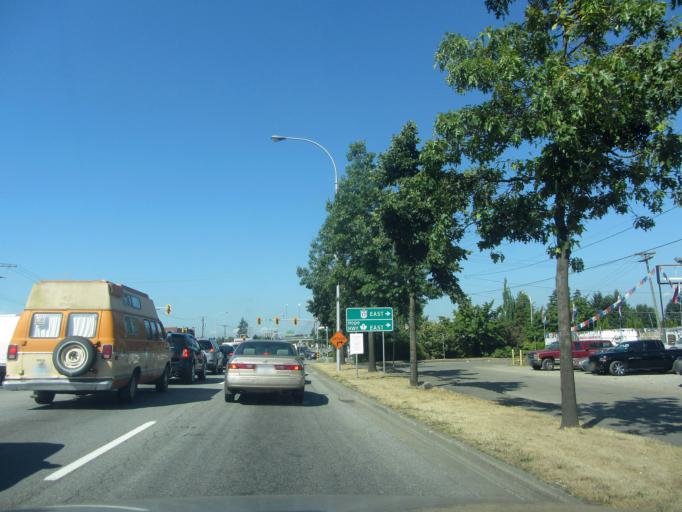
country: CA
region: British Columbia
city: New Westminster
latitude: 49.2065
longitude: -122.8661
